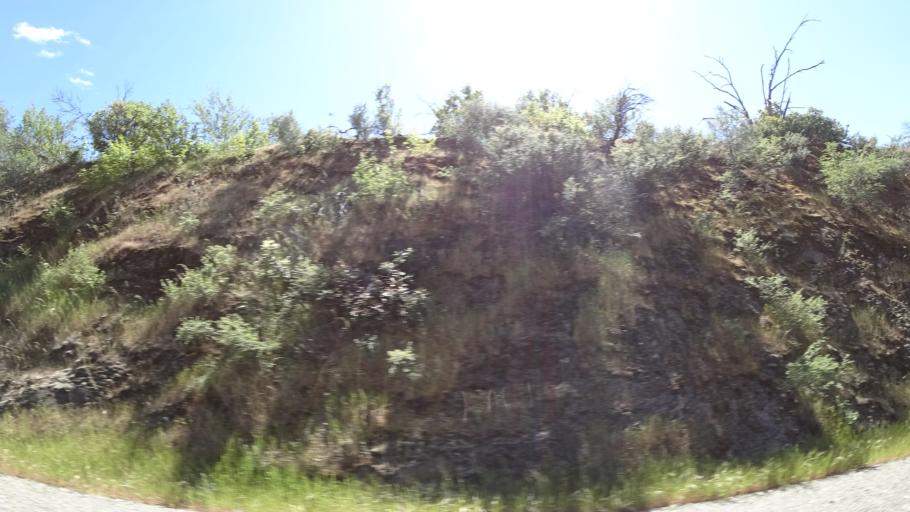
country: US
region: California
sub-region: Trinity County
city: Weaverville
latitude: 40.7354
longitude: -123.0114
